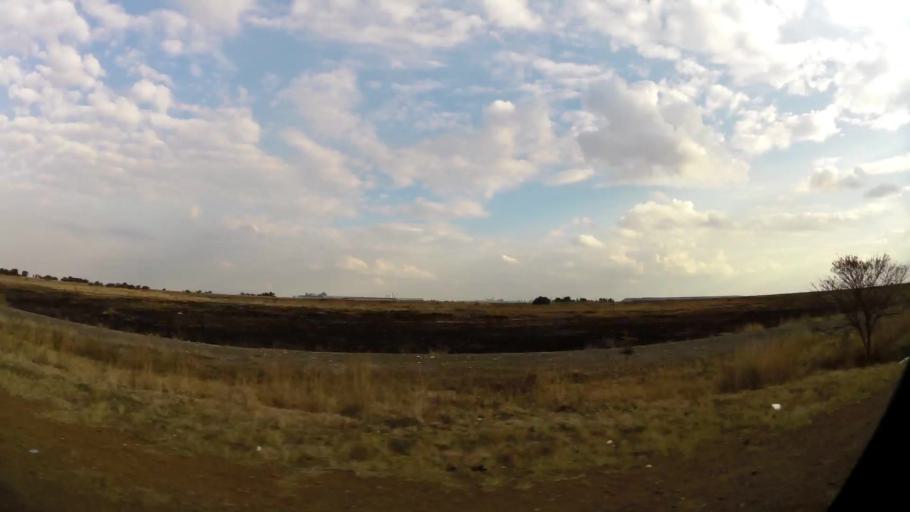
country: ZA
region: Gauteng
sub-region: Sedibeng District Municipality
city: Vanderbijlpark
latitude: -26.6188
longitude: 27.8436
